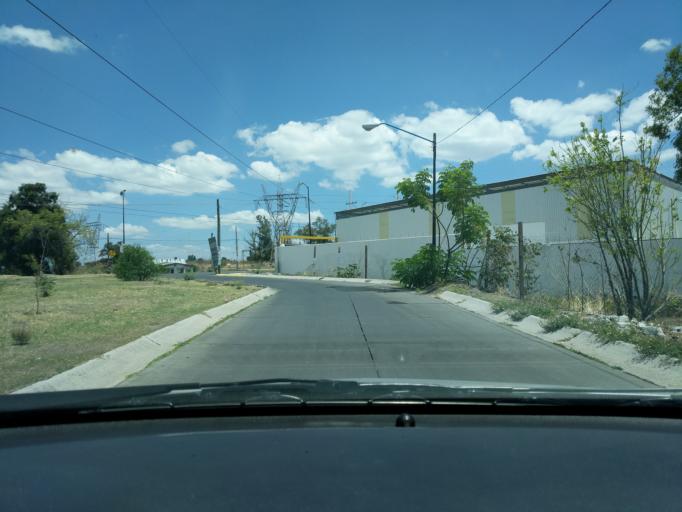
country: MX
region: Guanajuato
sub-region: Salamanca
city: El Divisador
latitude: 20.6030
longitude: -101.1757
